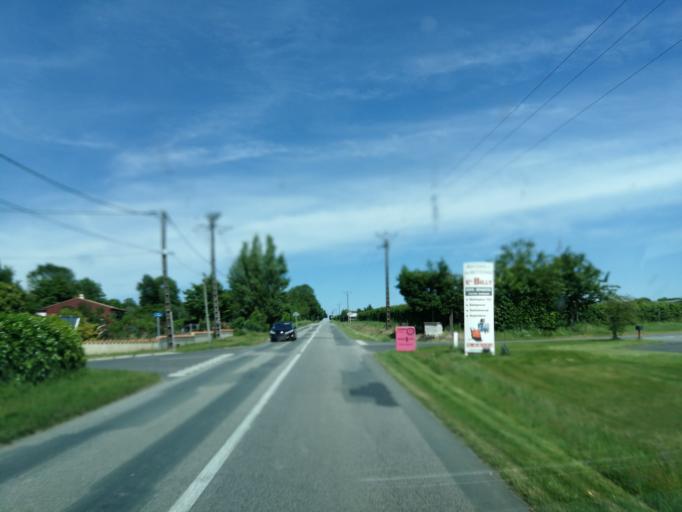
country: FR
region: Poitou-Charentes
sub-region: Departement des Deux-Sevres
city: Courlay
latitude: 46.8022
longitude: -0.5792
